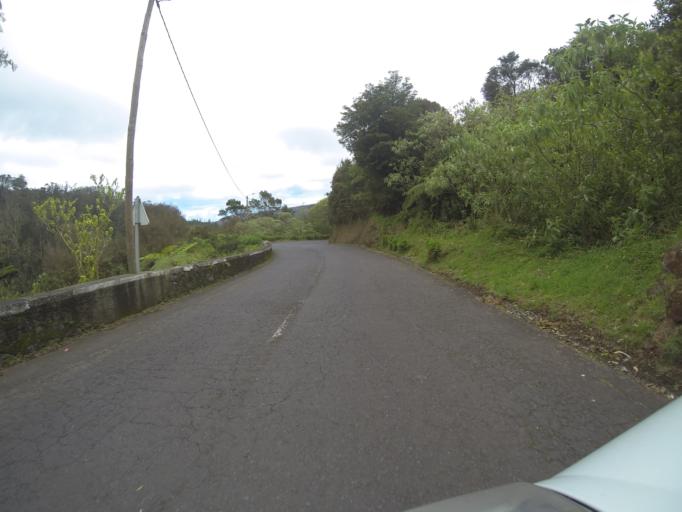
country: PT
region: Madeira
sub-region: Santa Cruz
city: Santa Cruz
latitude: 32.7427
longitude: -16.8257
